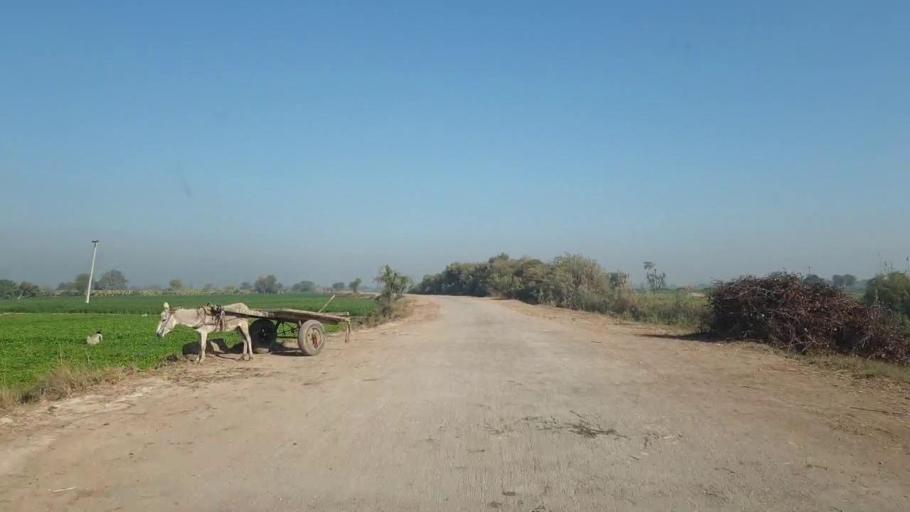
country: PK
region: Sindh
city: Shahdadpur
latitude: 25.9218
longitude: 68.5068
